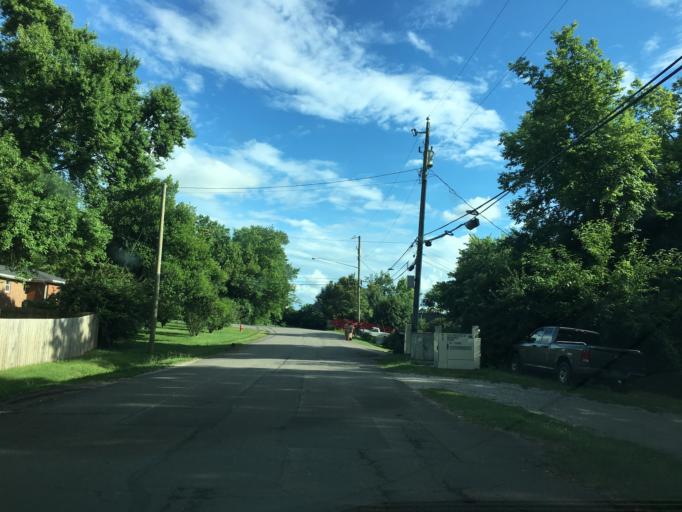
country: US
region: Tennessee
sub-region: Davidson County
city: Oak Hill
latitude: 36.0952
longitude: -86.7341
